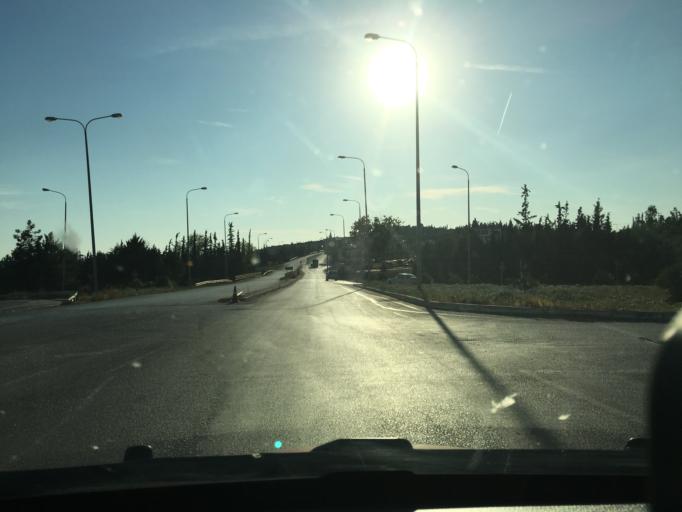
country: GR
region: Central Macedonia
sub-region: Nomos Chalkidikis
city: Nea Moudhania
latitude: 40.2434
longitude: 23.3008
